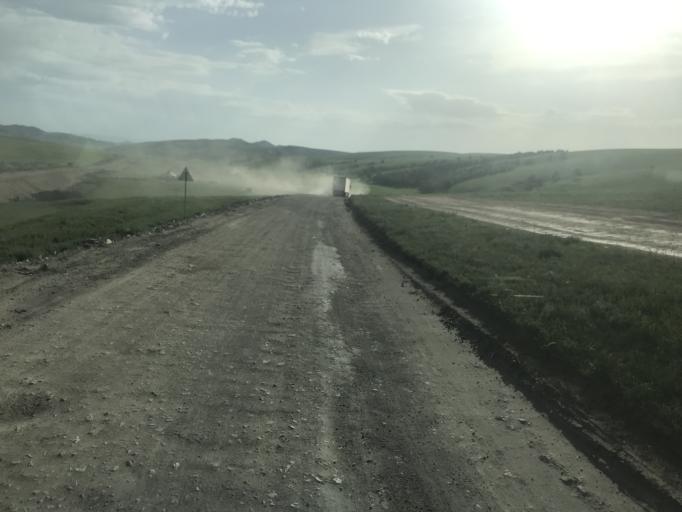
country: MN
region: Central Aimak
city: Javhlant
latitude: 48.6522
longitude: 106.1087
